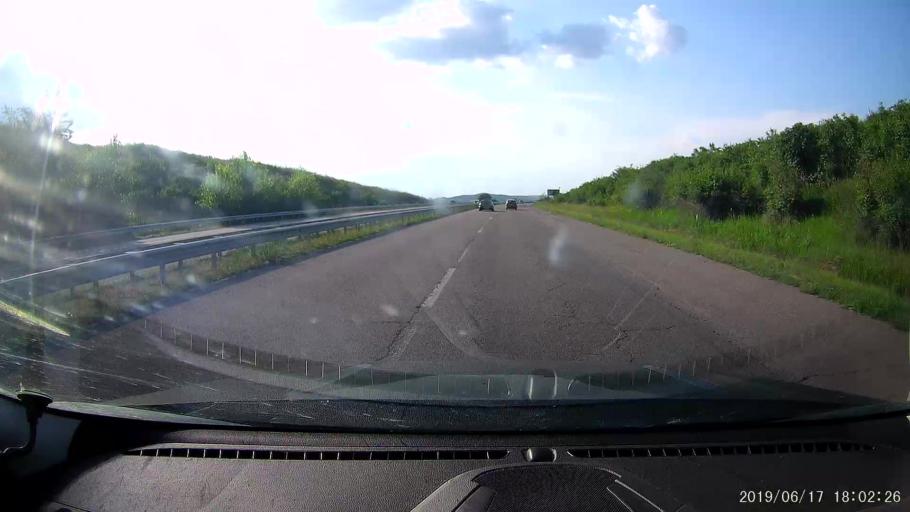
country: BG
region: Khaskovo
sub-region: Obshtina Svilengrad
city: Svilengrad
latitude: 41.7596
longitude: 26.2309
